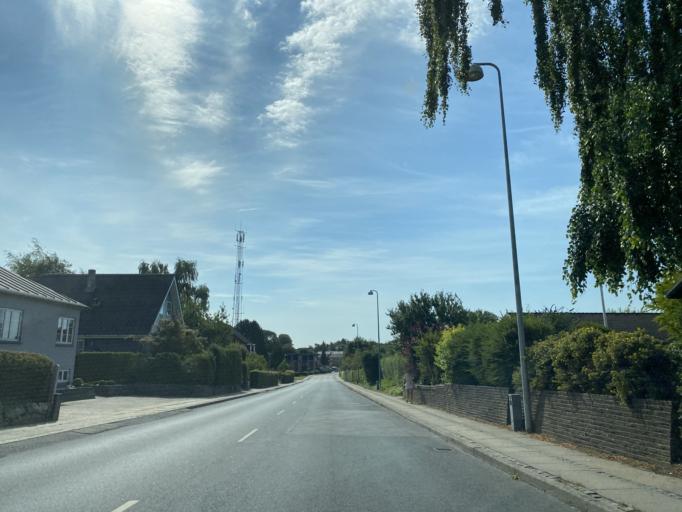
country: DK
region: Central Jutland
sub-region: Favrskov Kommune
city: Hammel
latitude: 56.2590
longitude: 9.8570
